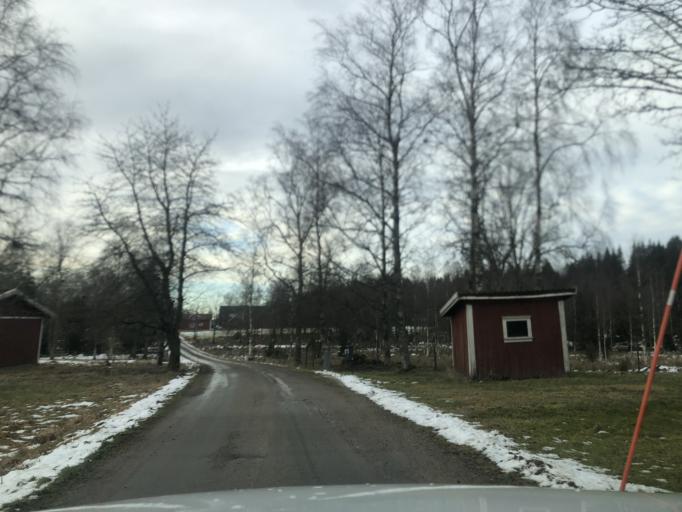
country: SE
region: Vaestra Goetaland
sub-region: Ulricehamns Kommun
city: Ulricehamn
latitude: 57.7993
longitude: 13.4970
